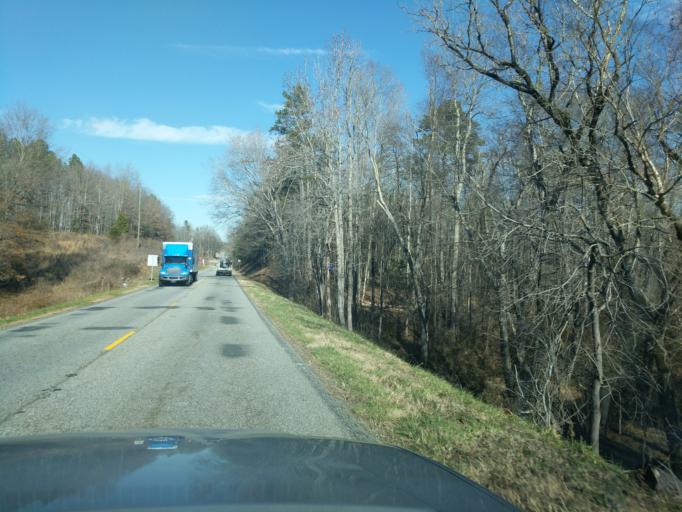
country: US
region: South Carolina
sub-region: Spartanburg County
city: Mayo
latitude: 35.1779
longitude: -81.8449
